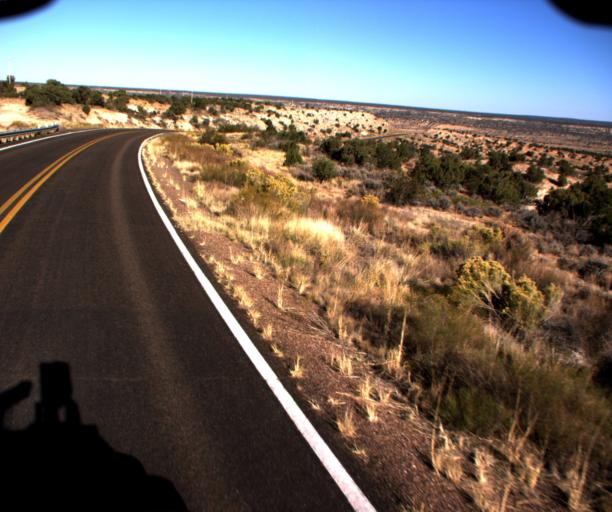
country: US
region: Arizona
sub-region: Navajo County
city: First Mesa
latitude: 35.7358
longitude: -110.1176
